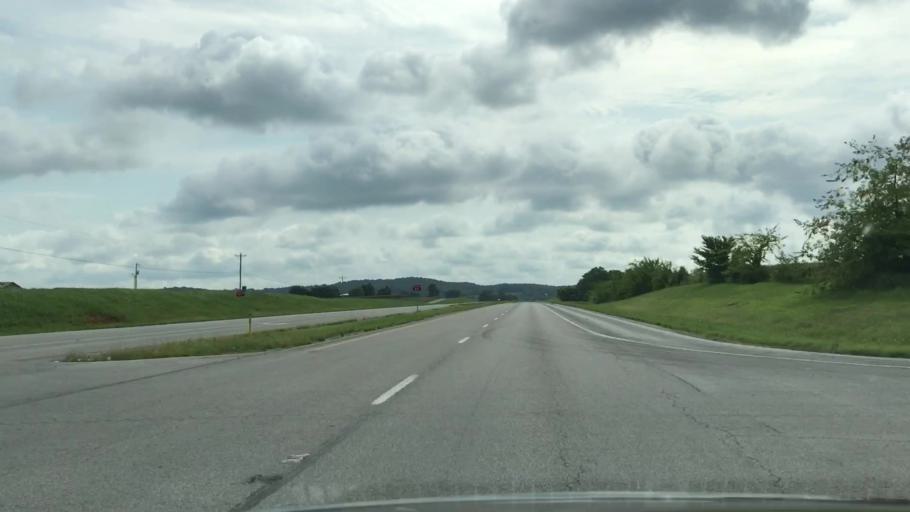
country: US
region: Kentucky
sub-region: Todd County
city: Elkton
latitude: 36.8415
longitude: -87.2602
